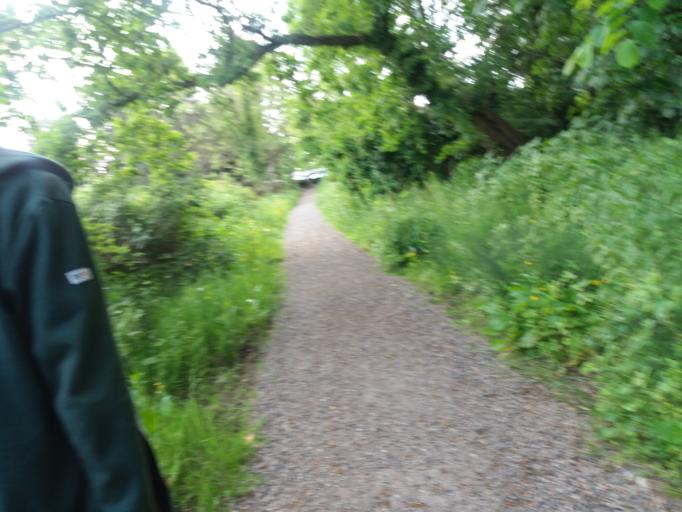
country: GB
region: England
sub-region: Lancashire
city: Euxton
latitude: 53.6503
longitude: -2.6608
